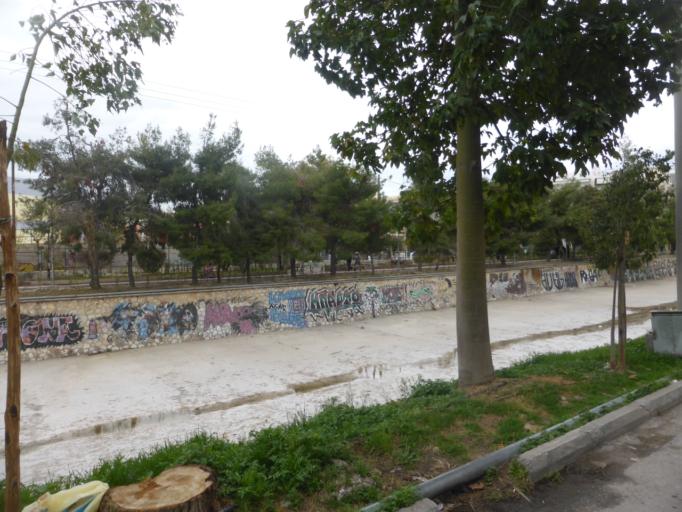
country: GR
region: Attica
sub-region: Nomarchia Athinas
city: Kallithea
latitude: 37.9528
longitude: 23.6893
